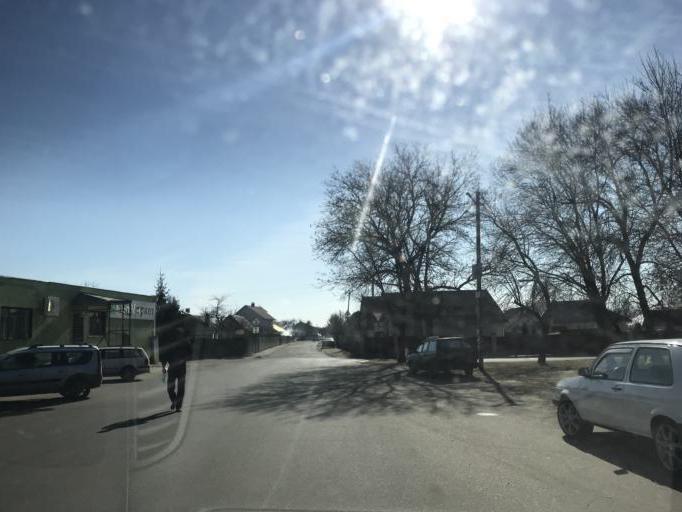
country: BY
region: Mogilev
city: Mahilyow
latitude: 53.9369
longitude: 30.3203
